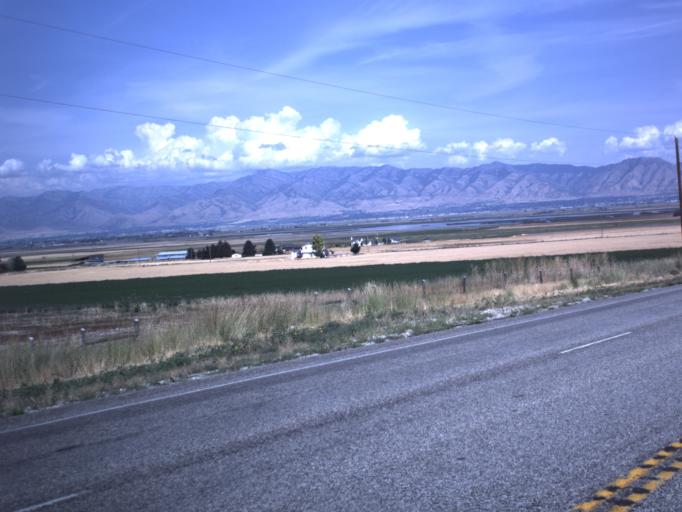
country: US
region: Utah
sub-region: Cache County
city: Mendon
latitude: 41.7543
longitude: -111.9943
